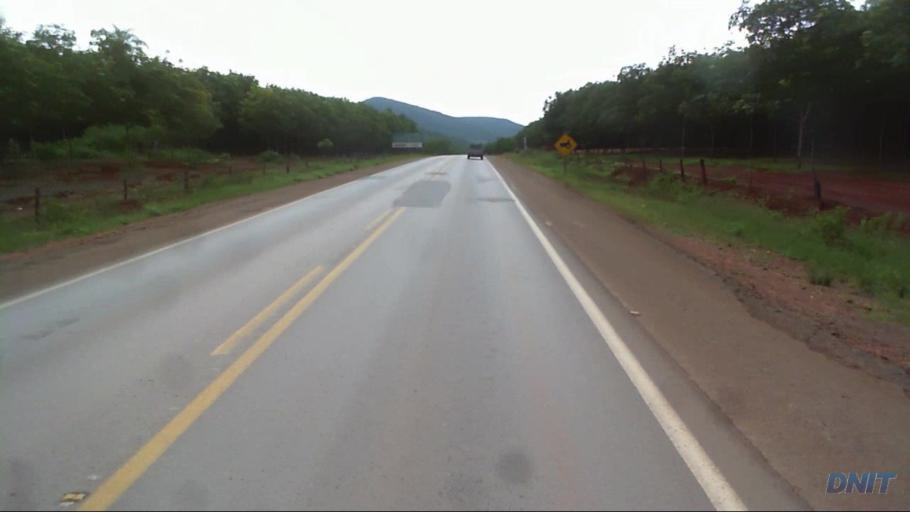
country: BR
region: Goias
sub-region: Barro Alto
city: Barro Alto
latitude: -14.8775
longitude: -48.9946
